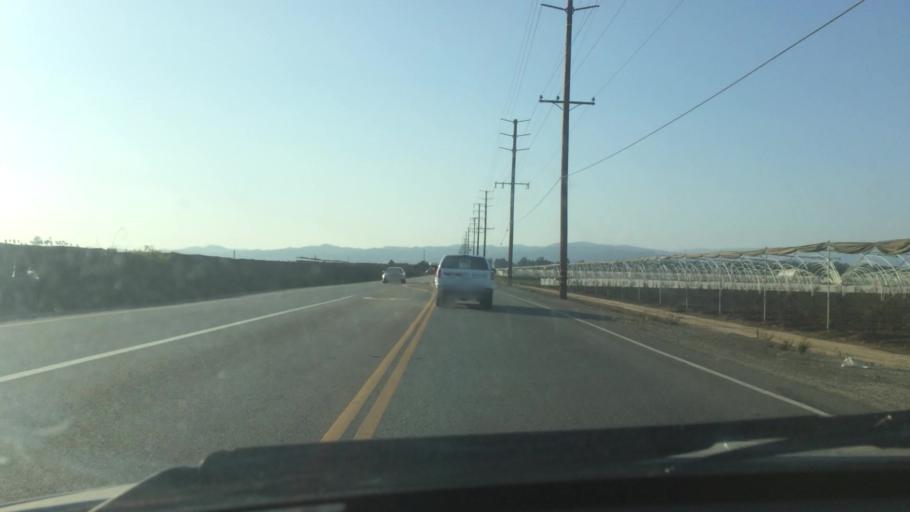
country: US
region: California
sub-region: Ventura County
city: Saticoy
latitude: 34.2599
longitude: -119.1148
